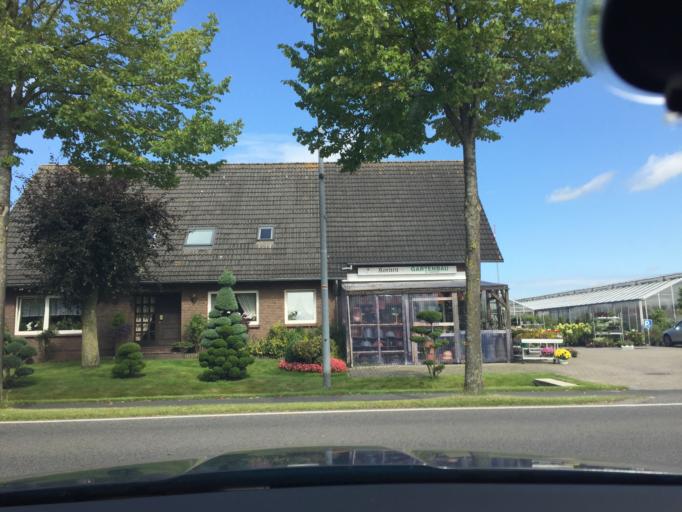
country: DE
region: Lower Saxony
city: Rechtsupweg
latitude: 53.5162
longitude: 7.3735
